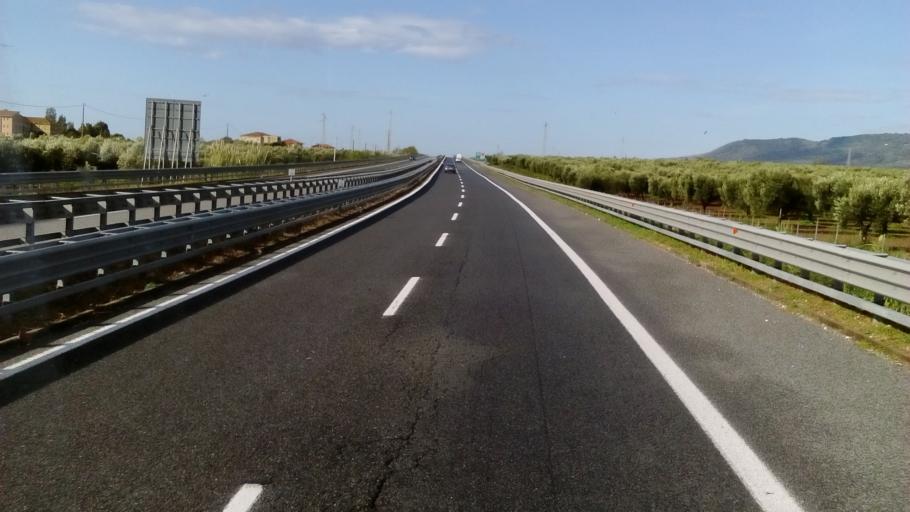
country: IT
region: Calabria
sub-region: Provincia di Catanzaro
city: Santa Eufemia Lamezia
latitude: 38.9239
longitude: 16.2581
